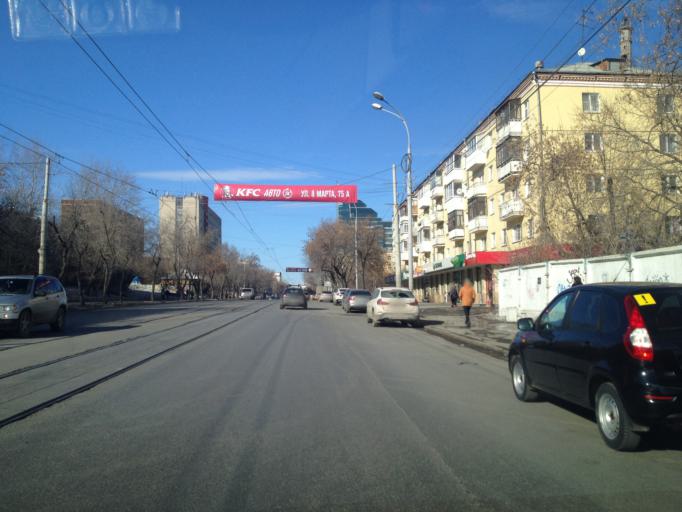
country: RU
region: Sverdlovsk
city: Yekaterinburg
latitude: 56.8194
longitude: 60.6061
